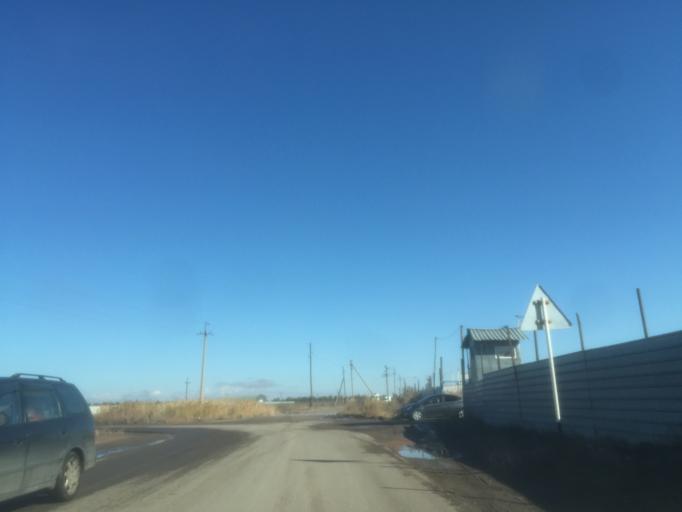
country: KZ
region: Astana Qalasy
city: Astana
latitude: 51.2138
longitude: 71.3553
